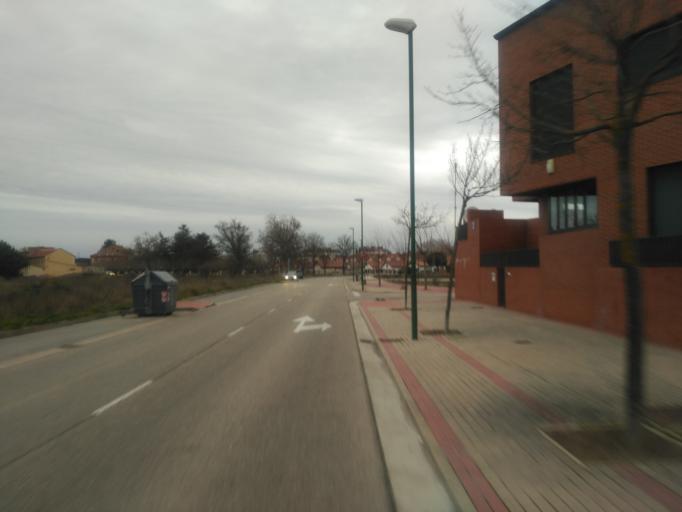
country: ES
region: Castille and Leon
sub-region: Provincia de Burgos
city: Villagonzalo-Pedernales
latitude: 42.3415
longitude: -3.7365
